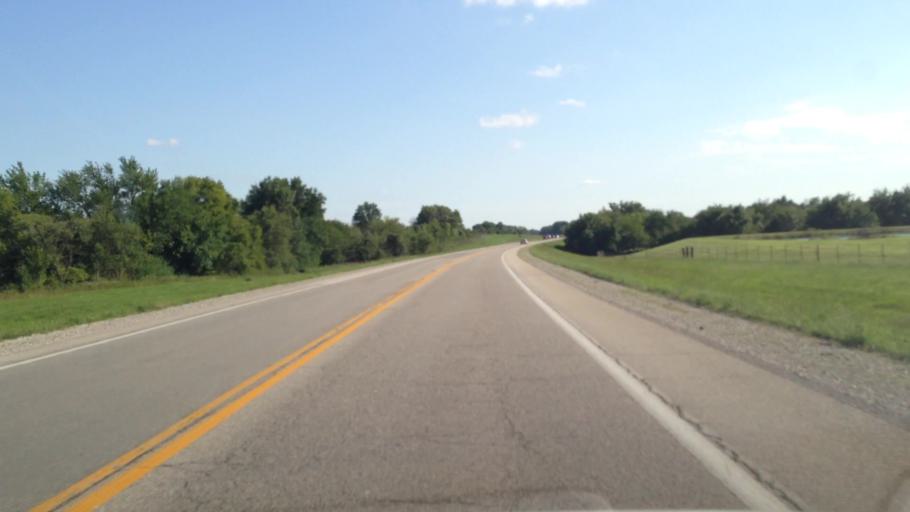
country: US
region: Kansas
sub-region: Crawford County
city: Arma
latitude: 37.5385
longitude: -94.7096
